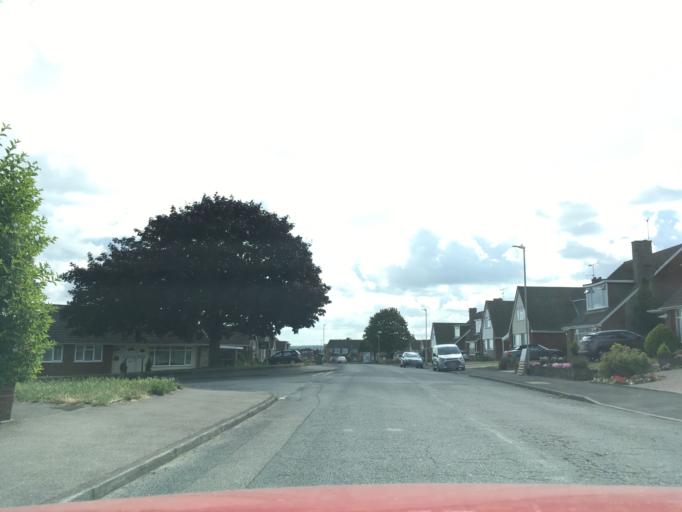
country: GB
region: England
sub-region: Kent
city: Maidstone
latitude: 51.2849
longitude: 0.4985
